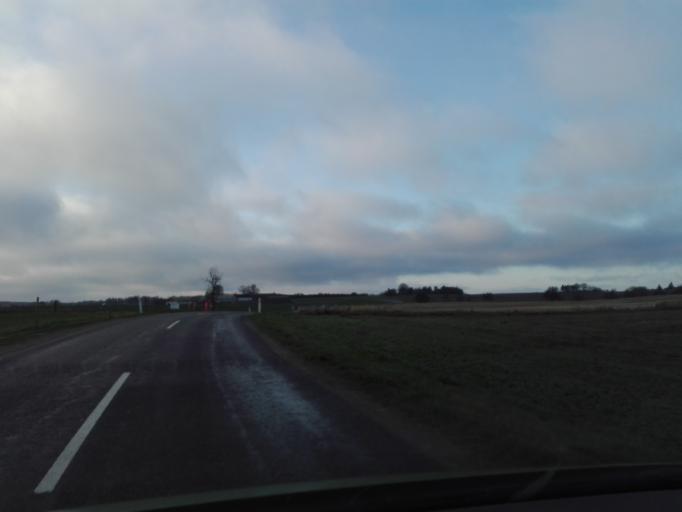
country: DK
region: Central Jutland
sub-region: Arhus Kommune
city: Solbjerg
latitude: 56.0309
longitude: 10.0548
